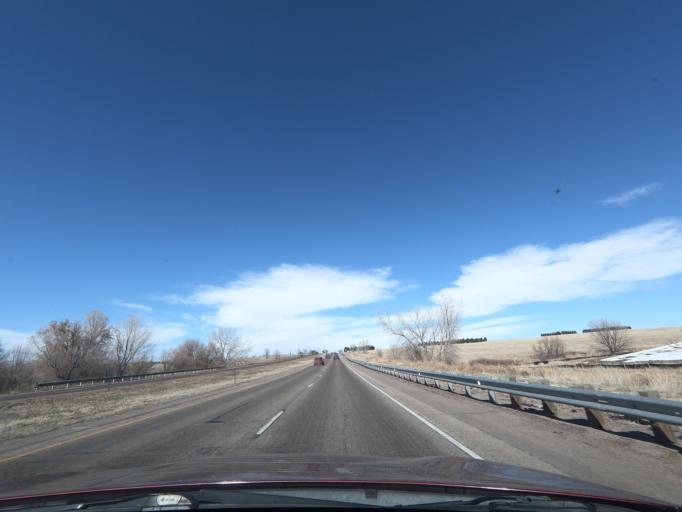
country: US
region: Colorado
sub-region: El Paso County
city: Security-Widefield
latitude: 38.7749
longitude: -104.7207
